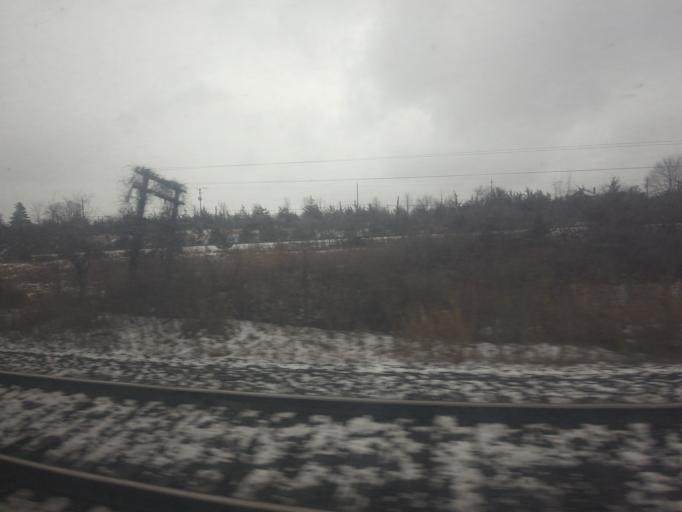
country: CA
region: Ontario
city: Quinte West
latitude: 44.0835
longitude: -77.6410
